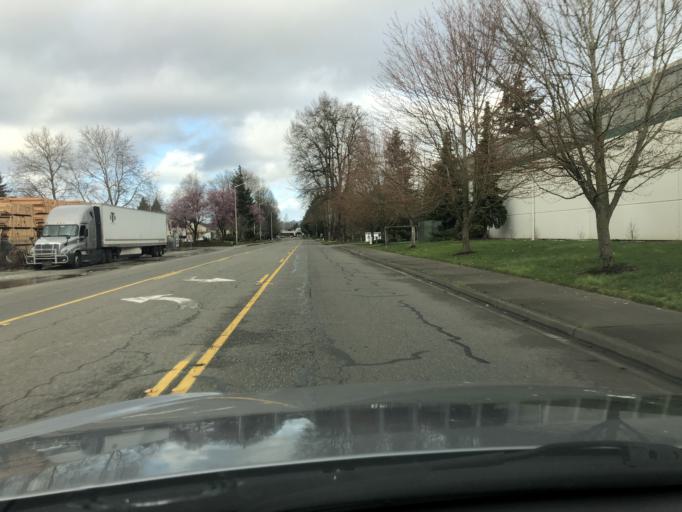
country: US
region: Washington
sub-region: King County
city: Tukwila
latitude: 47.4369
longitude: -122.2438
